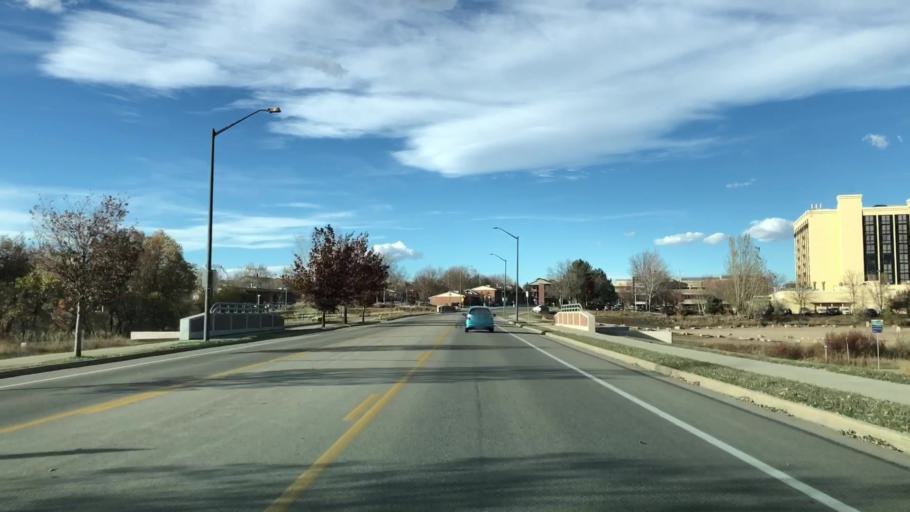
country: US
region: Colorado
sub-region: Larimer County
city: Fort Collins
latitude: 40.5638
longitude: -105.0836
